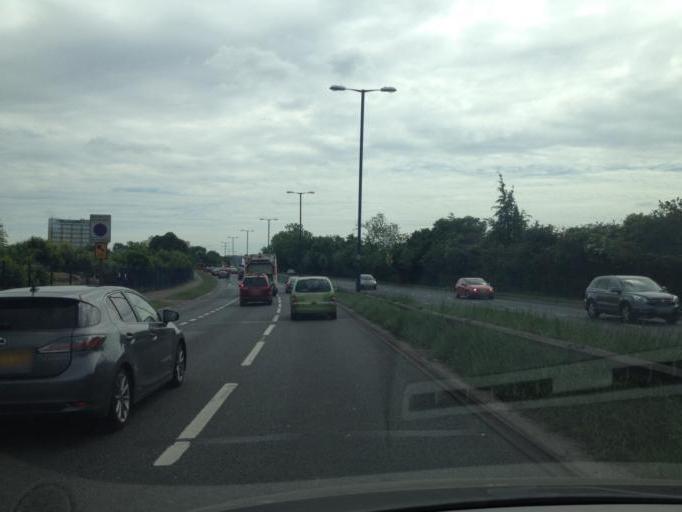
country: GB
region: England
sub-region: Greater London
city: Ealing Broadway
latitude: 51.5314
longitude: -0.3066
